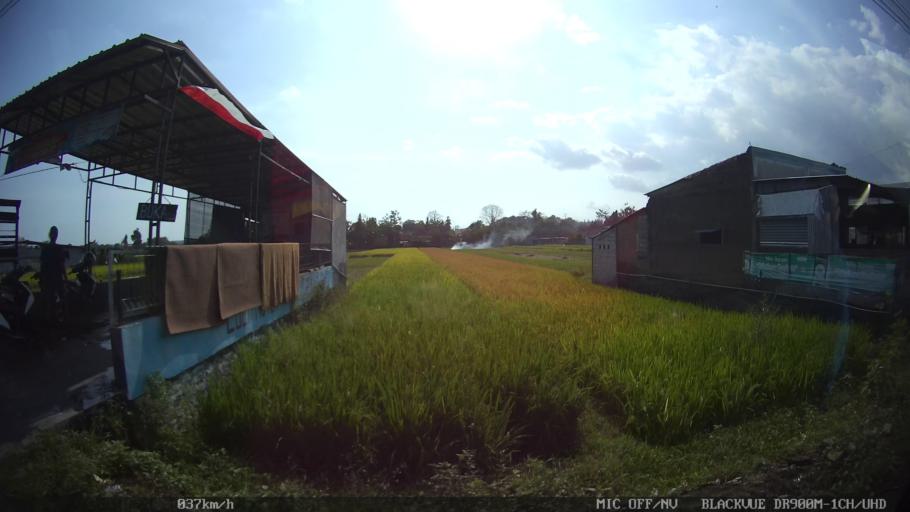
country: ID
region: Daerah Istimewa Yogyakarta
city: Kasihan
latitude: -7.8435
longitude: 110.3434
